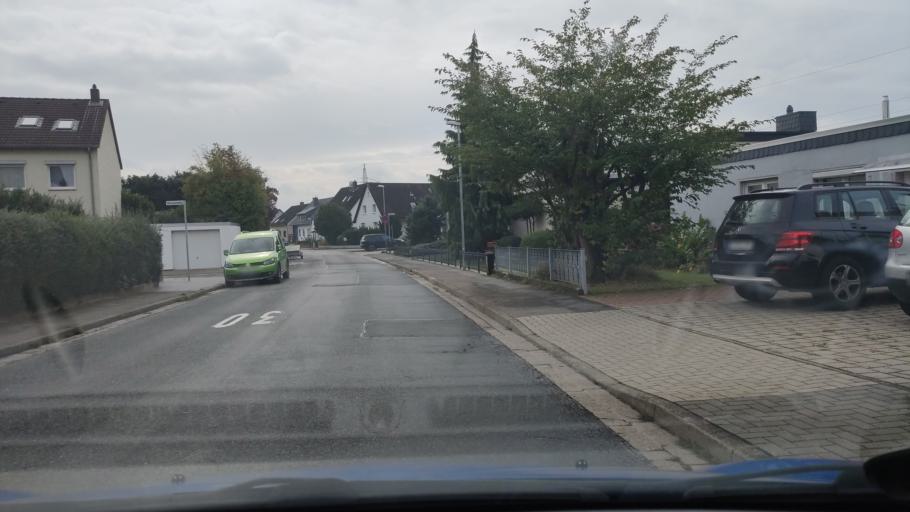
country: DE
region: Lower Saxony
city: Ronnenberg
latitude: 52.3694
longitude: 9.6476
